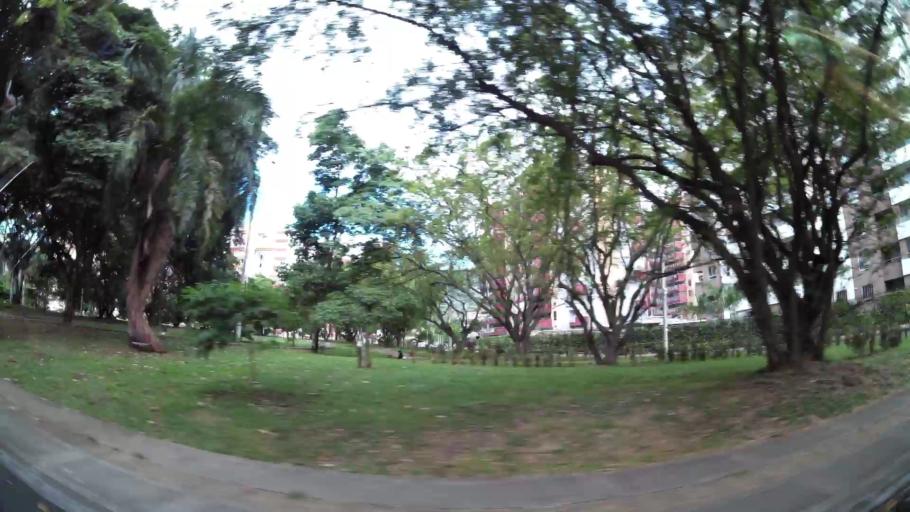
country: CO
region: Valle del Cauca
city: Cali
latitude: 3.4911
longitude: -76.5203
